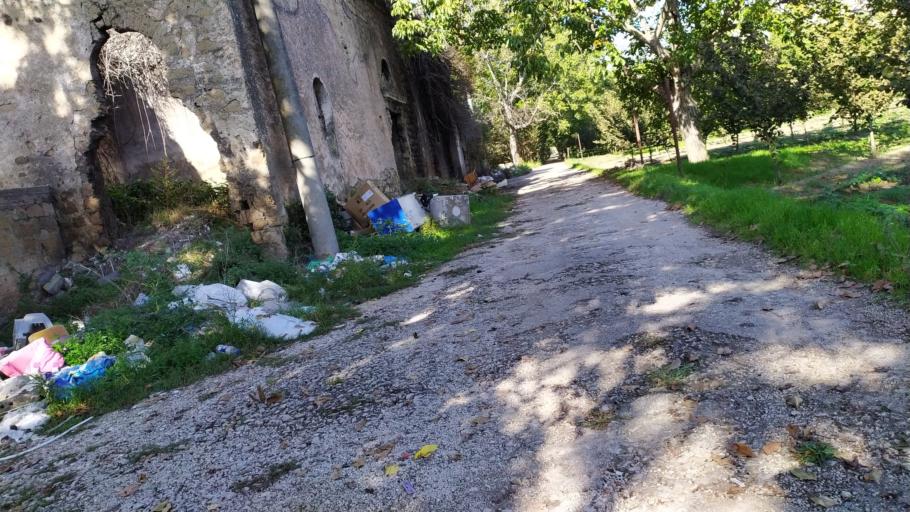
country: IT
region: Campania
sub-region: Provincia di Napoli
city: Camposano
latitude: 40.9633
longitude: 14.5180
